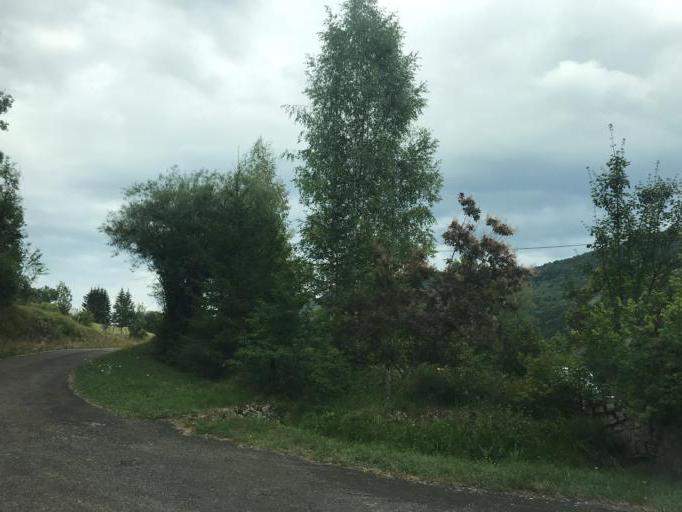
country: FR
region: Franche-Comte
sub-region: Departement du Jura
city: Longchaumois
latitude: 46.4678
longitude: 5.8958
